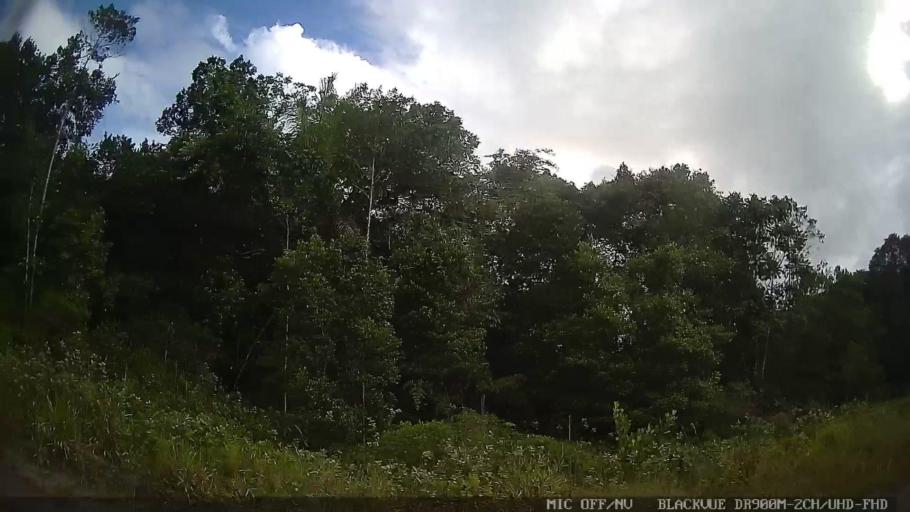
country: BR
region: Sao Paulo
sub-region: Itanhaem
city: Itanhaem
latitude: -24.1792
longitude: -46.9213
